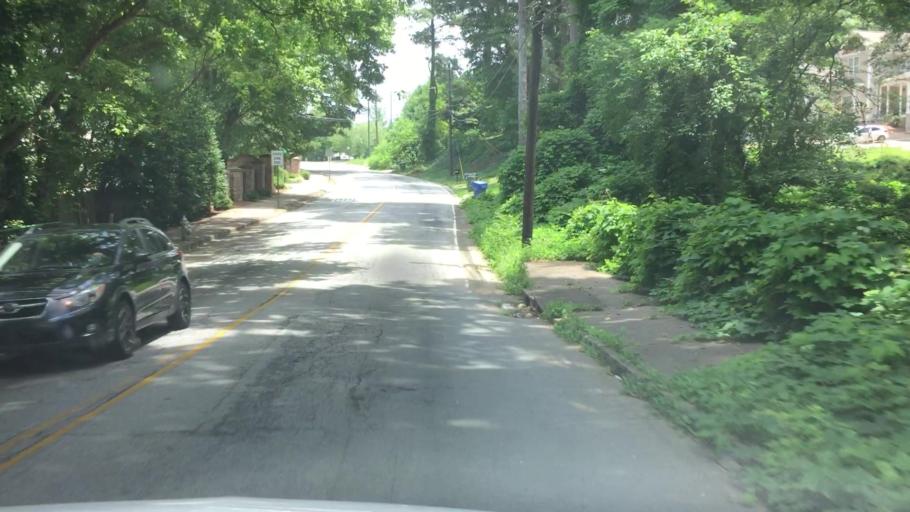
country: US
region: Georgia
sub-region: DeKalb County
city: Gresham Park
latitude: 33.7156
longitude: -84.3524
